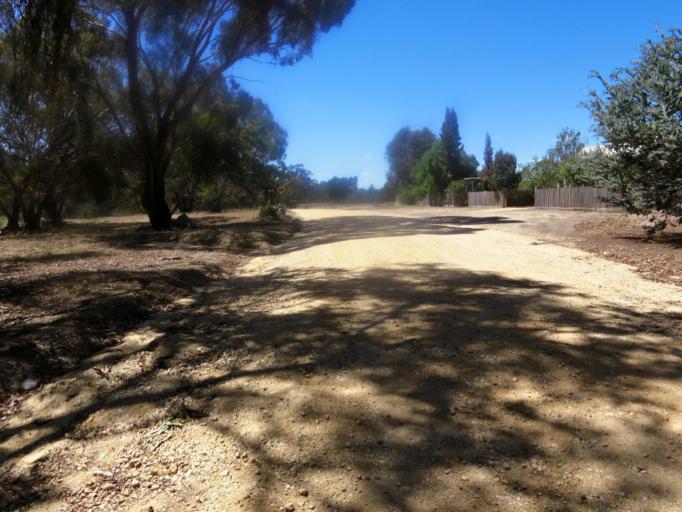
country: AU
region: Victoria
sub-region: Mount Alexander
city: Castlemaine
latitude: -36.9921
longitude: 144.0815
